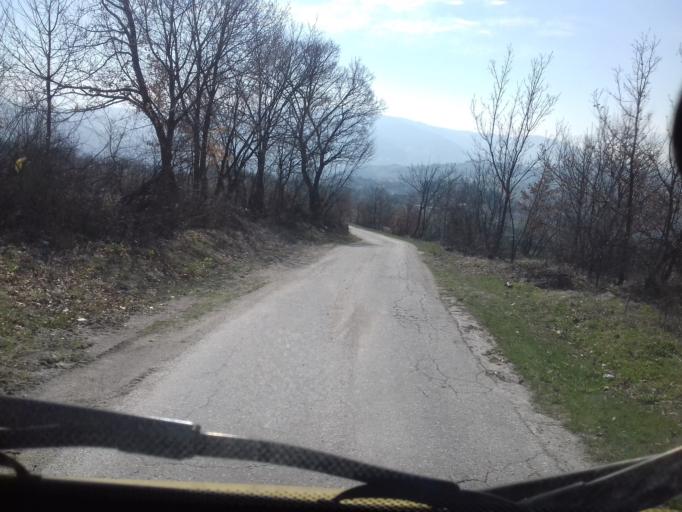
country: BA
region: Federation of Bosnia and Herzegovina
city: Travnik
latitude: 44.2479
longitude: 17.7242
